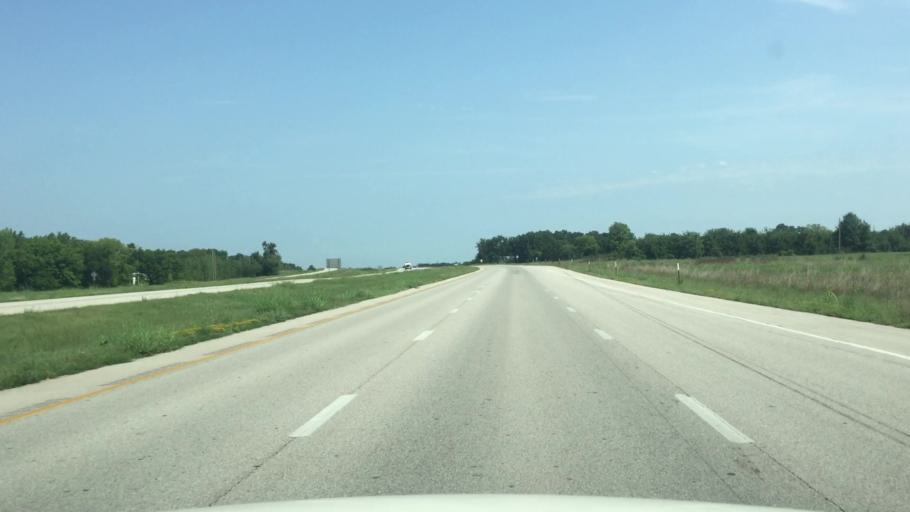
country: US
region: Kansas
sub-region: Montgomery County
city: Coffeyville
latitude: 37.0507
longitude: -95.5811
